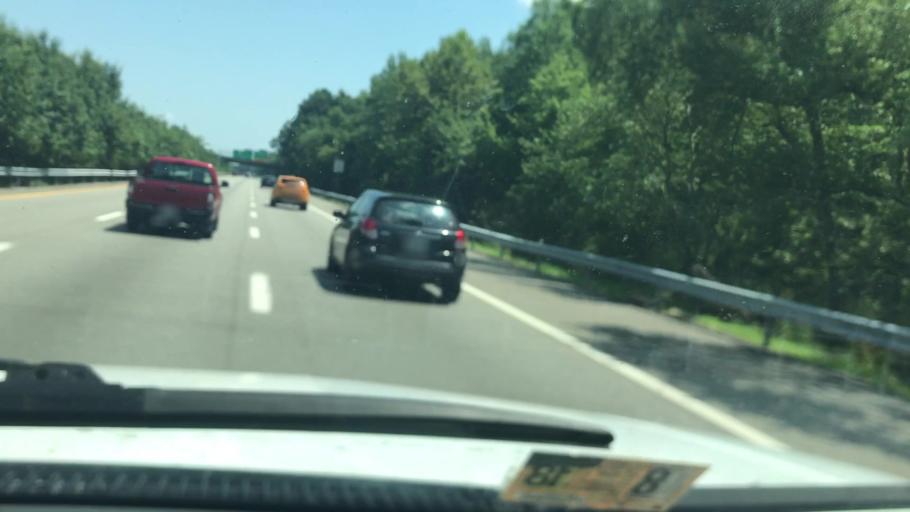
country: US
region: Virginia
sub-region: Henrico County
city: Highland Springs
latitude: 37.5318
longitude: -77.3488
